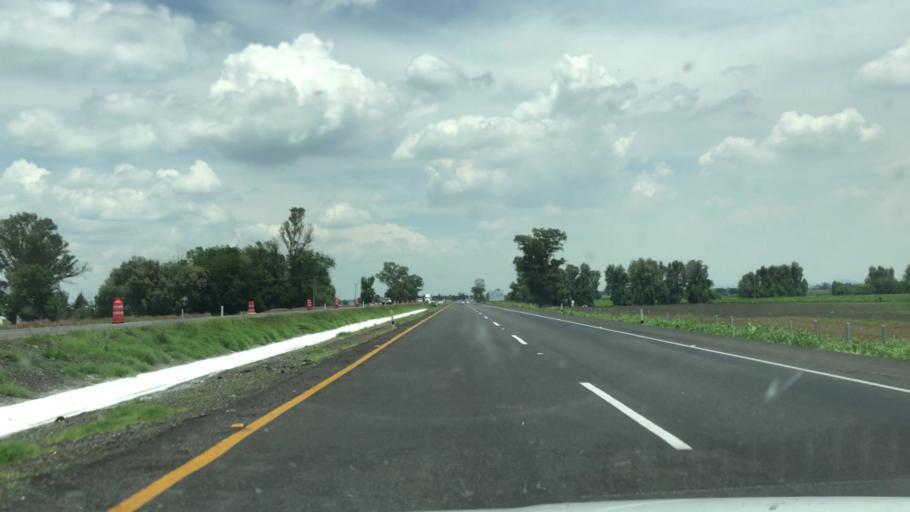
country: MX
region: Guanajuato
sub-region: Irapuato
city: Cuarta Brigada
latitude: 20.6427
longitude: -101.2695
